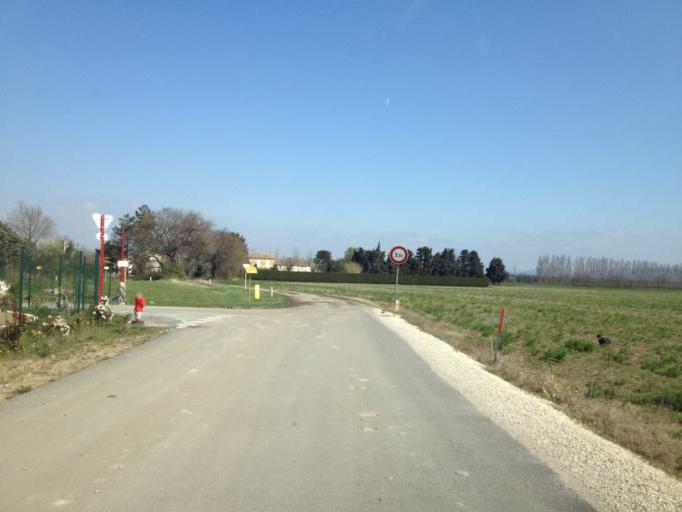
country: FR
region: Provence-Alpes-Cote d'Azur
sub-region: Departement du Vaucluse
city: Jonquieres
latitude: 44.1226
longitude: 4.9120
